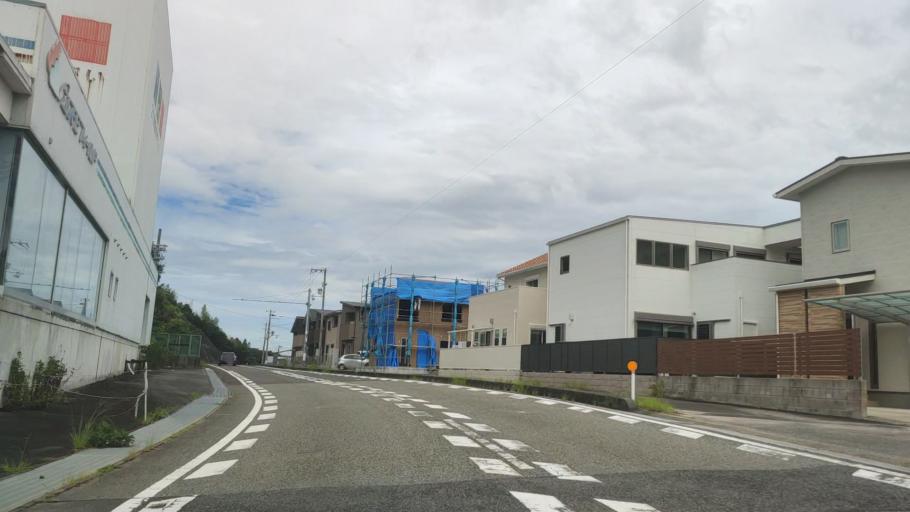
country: JP
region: Wakayama
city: Tanabe
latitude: 33.6872
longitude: 135.3891
